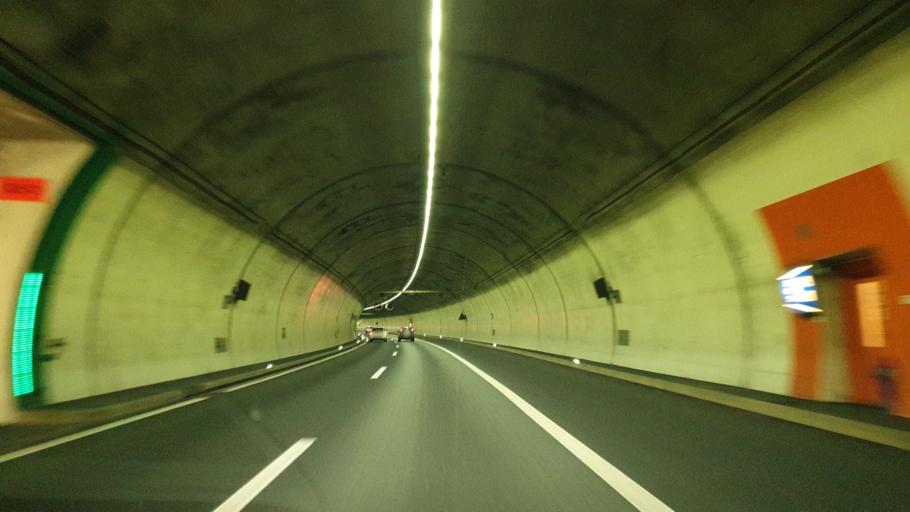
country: CH
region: Zurich
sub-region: Bezirk Dietikon
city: Birmensdorf
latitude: 47.3537
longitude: 8.4246
